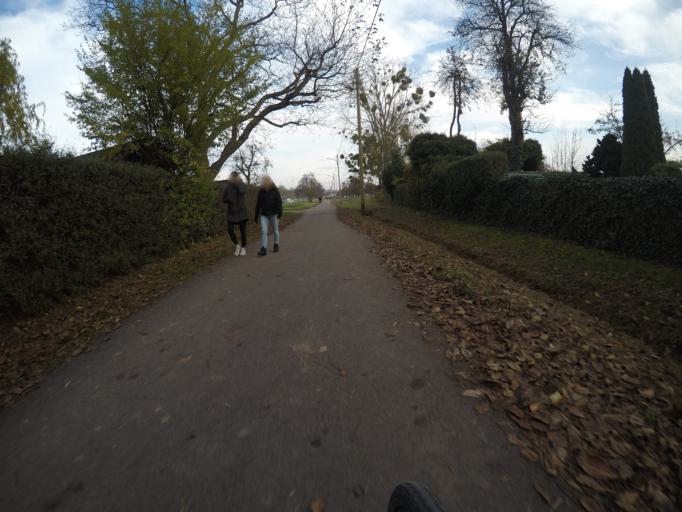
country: DE
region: Baden-Wuerttemberg
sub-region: Regierungsbezirk Stuttgart
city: Leinfelden-Echterdingen
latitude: 48.6894
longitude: 9.1484
